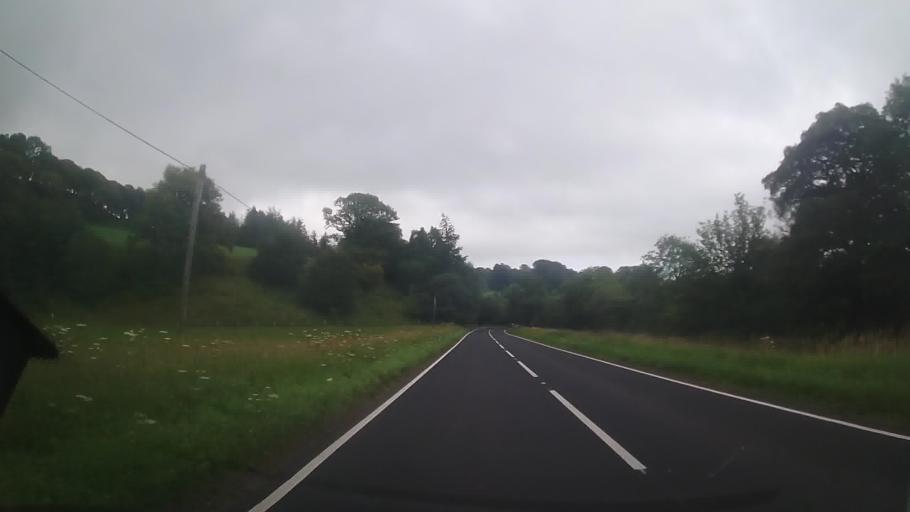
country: GB
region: Wales
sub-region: Conwy
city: Betws-y-Coed
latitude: 53.0561
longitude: -3.7471
